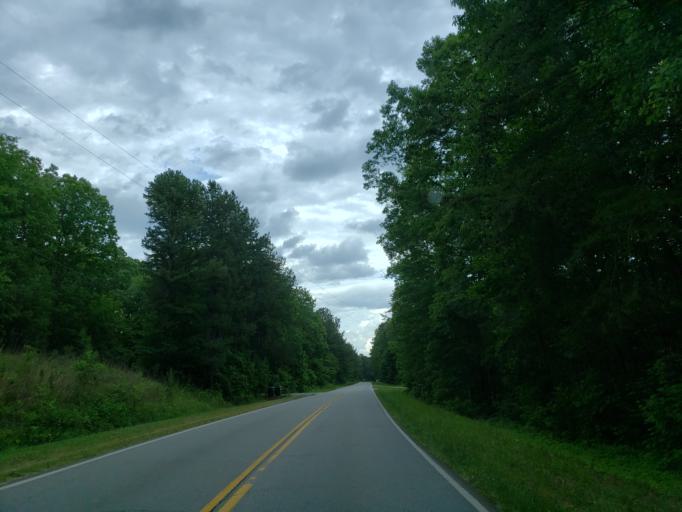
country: US
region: Georgia
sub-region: Polk County
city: Rockmart
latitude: 33.9474
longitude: -85.0458
